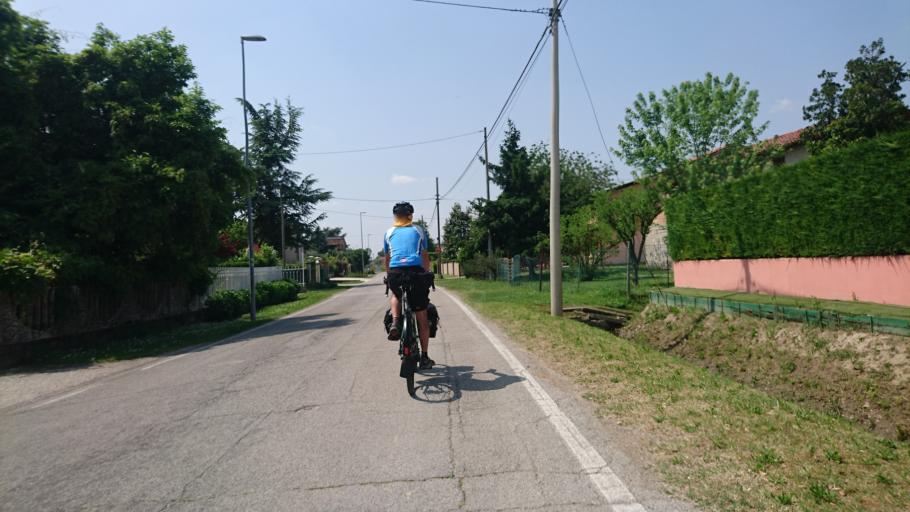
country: IT
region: Veneto
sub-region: Provincia di Venezia
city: Camponogara
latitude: 45.3721
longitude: 12.1032
